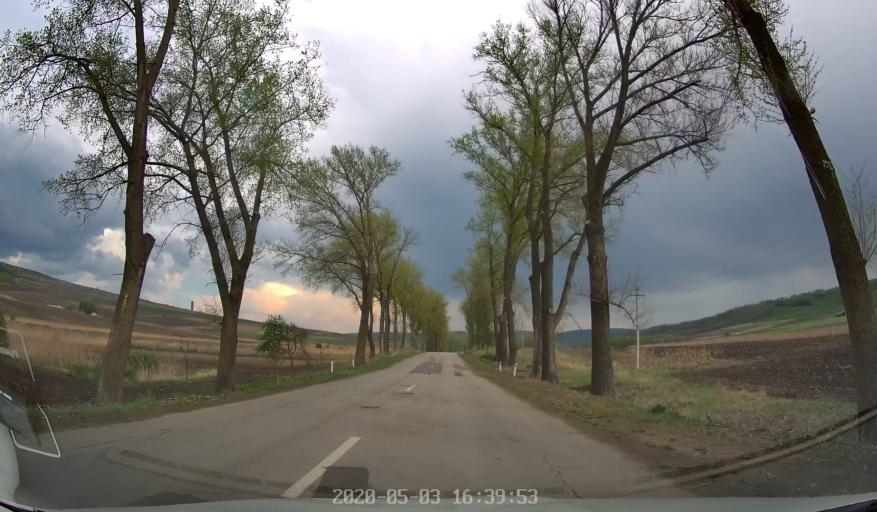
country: MD
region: Stinga Nistrului
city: Bucovat
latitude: 47.1793
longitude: 28.3824
